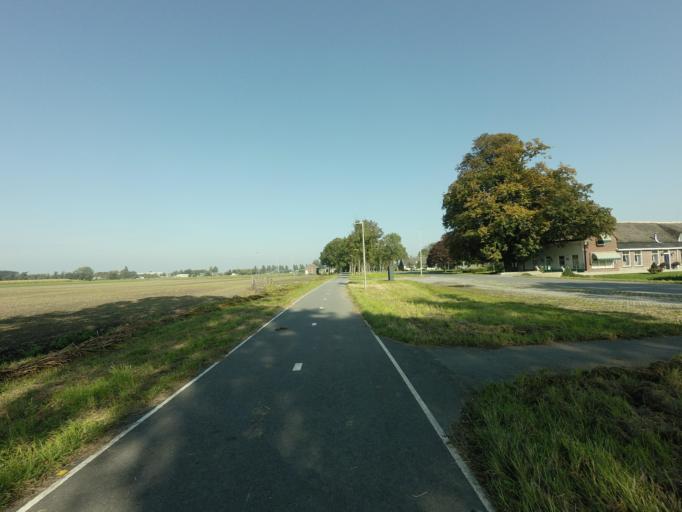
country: NL
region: Utrecht
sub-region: Gemeente Vianen
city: Vianen
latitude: 51.9529
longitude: 5.1479
